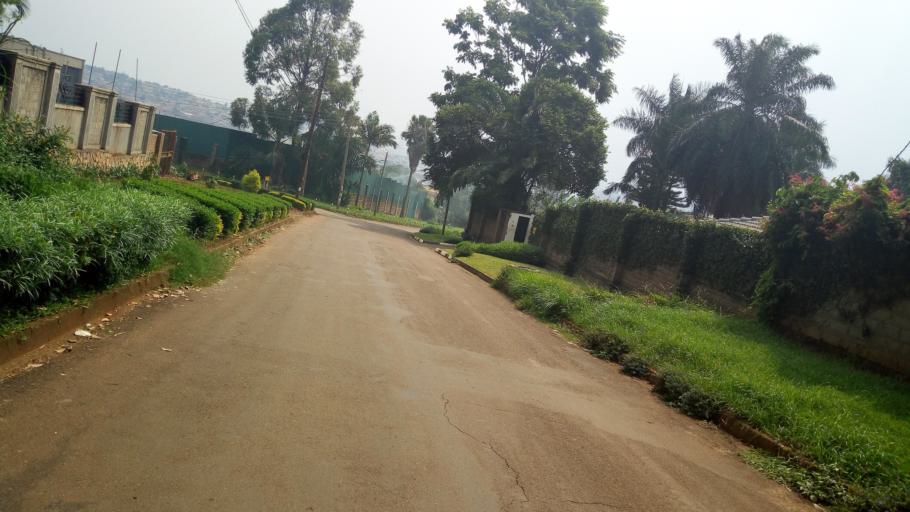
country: UG
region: Central Region
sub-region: Kampala District
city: Kampala
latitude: 0.3149
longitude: 32.6195
